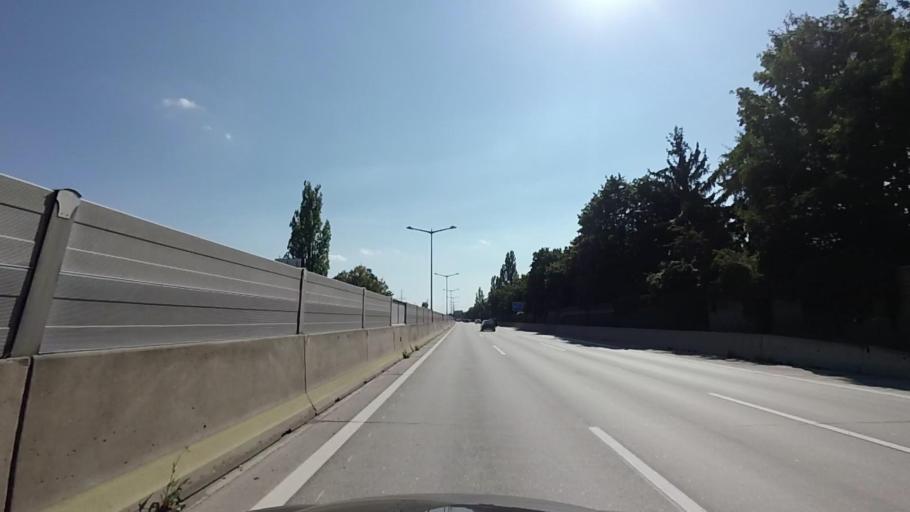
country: AT
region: Styria
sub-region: Politischer Bezirk Graz-Umgebung
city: Seiersberg
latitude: 47.0233
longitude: 15.4111
